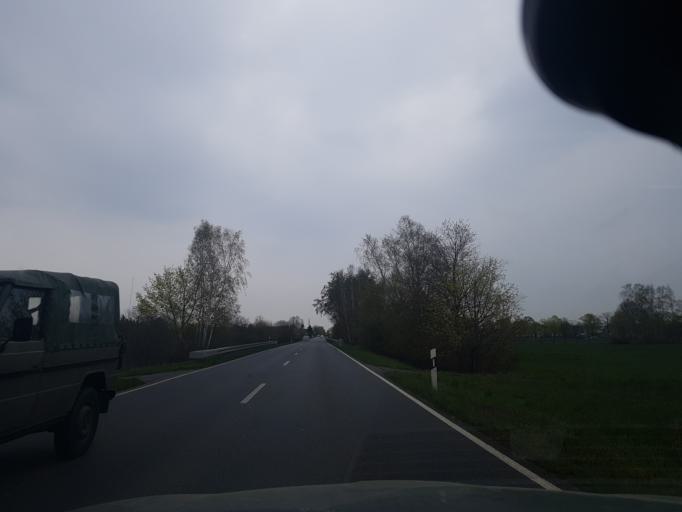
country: DE
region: Brandenburg
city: Hohenleipisch
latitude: 51.4704
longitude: 13.5595
